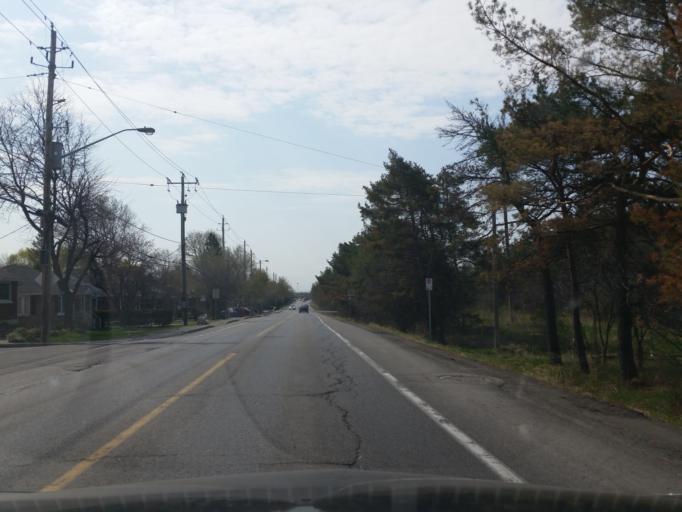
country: CA
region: Ontario
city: Ottawa
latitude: 45.4426
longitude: -75.6130
